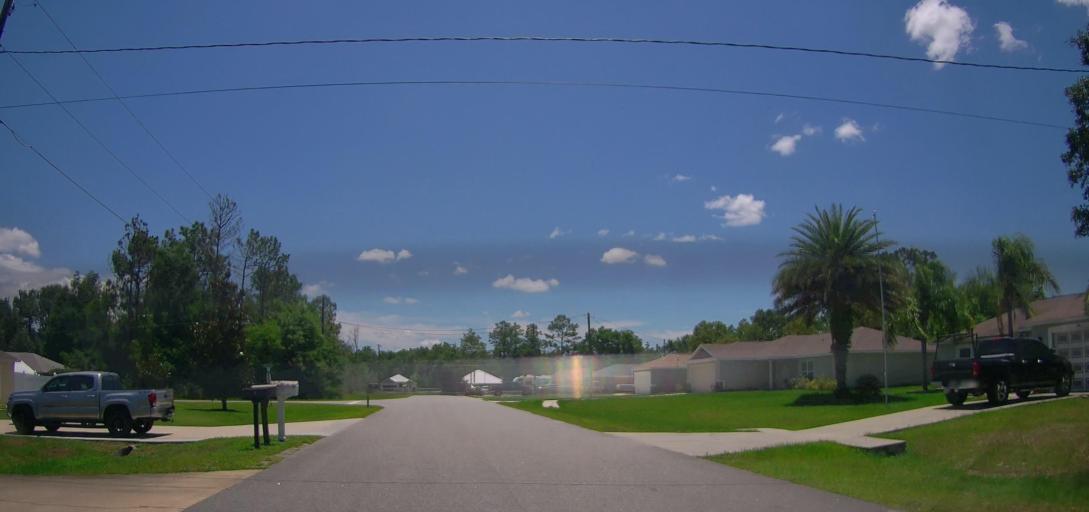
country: US
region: Florida
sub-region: Marion County
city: Silver Springs Shores
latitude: 29.1380
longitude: -82.0224
